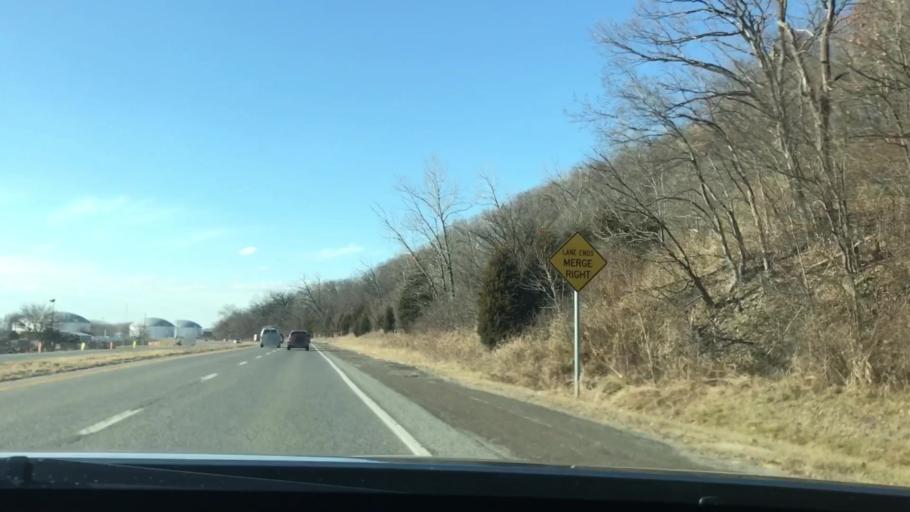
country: US
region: Missouri
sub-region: Platte County
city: Parkville
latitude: 39.1783
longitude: -94.6504
